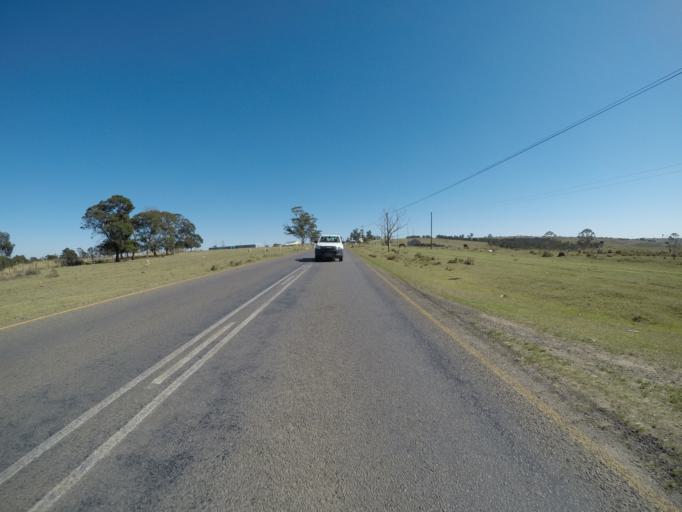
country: ZA
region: Eastern Cape
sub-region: OR Tambo District Municipality
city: Mthatha
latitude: -31.7988
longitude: 28.7457
